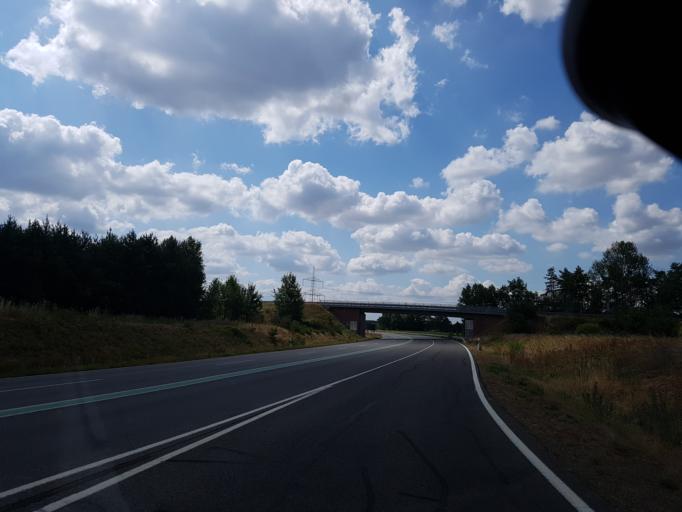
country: DE
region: Brandenburg
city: Drebkau
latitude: 51.6637
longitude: 14.2411
